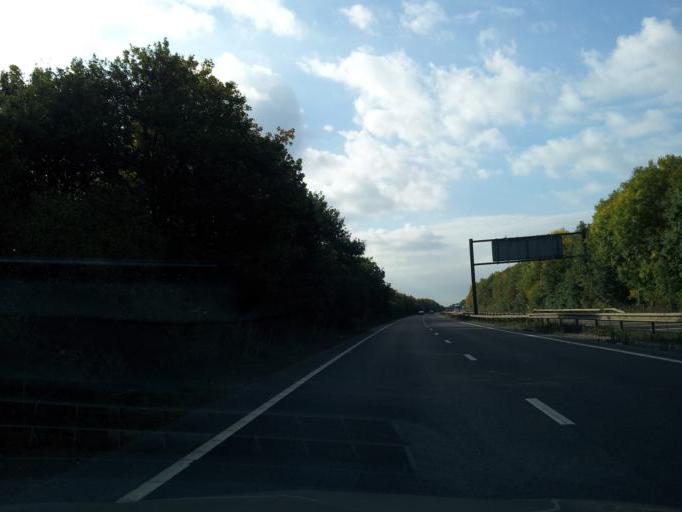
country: GB
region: England
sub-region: Northamptonshire
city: Blisworth
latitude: 52.2044
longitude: -0.9381
